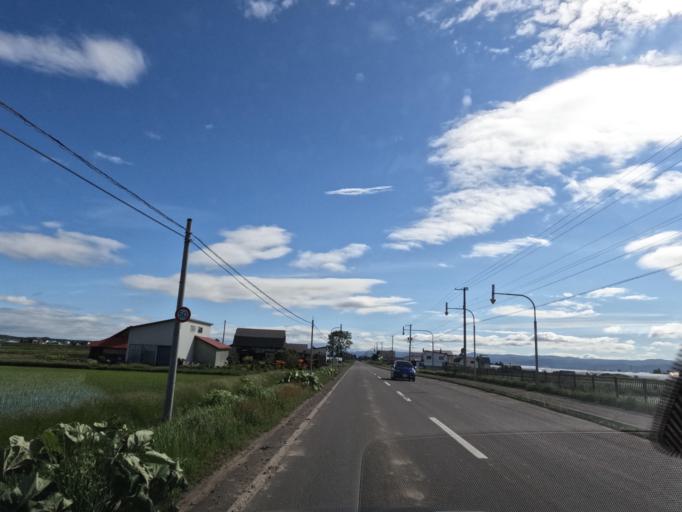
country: JP
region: Hokkaido
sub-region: Asahikawa-shi
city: Asahikawa
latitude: 43.7133
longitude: 142.5242
